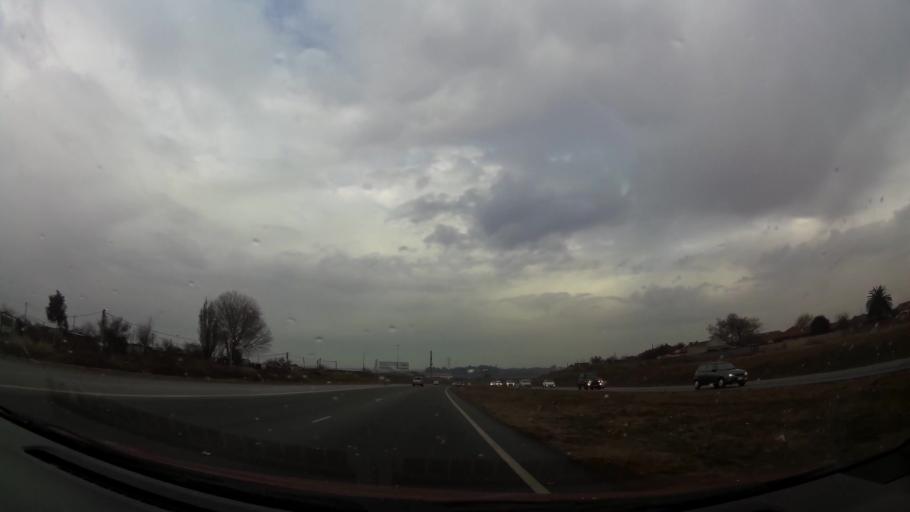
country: ZA
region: Gauteng
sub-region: City of Johannesburg Metropolitan Municipality
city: Soweto
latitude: -26.3051
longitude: 27.8942
